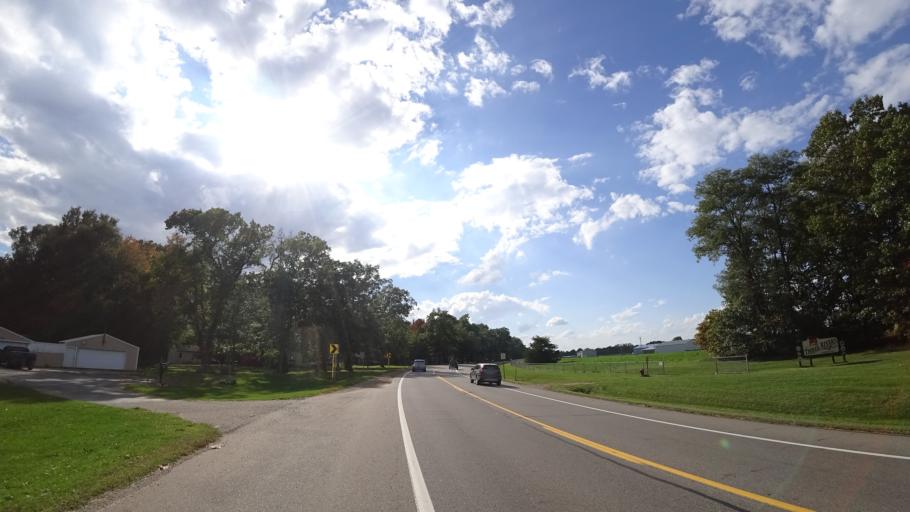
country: US
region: Michigan
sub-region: Saint Joseph County
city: Three Rivers
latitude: 41.9552
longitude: -85.5858
